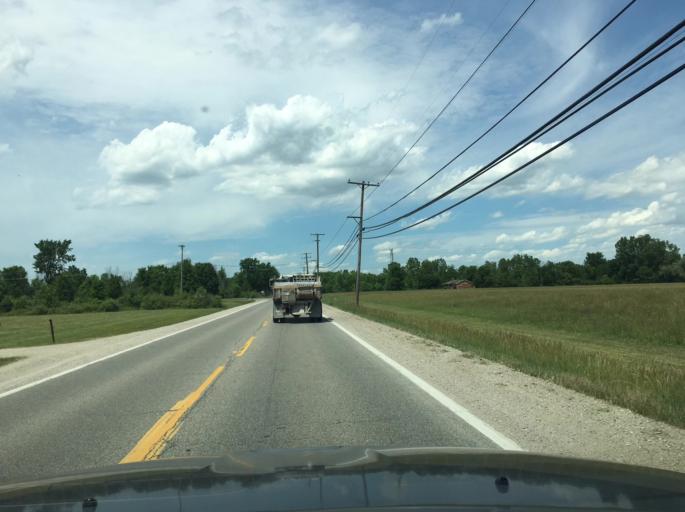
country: US
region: Michigan
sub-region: Macomb County
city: Shelby
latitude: 42.7186
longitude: -82.9596
